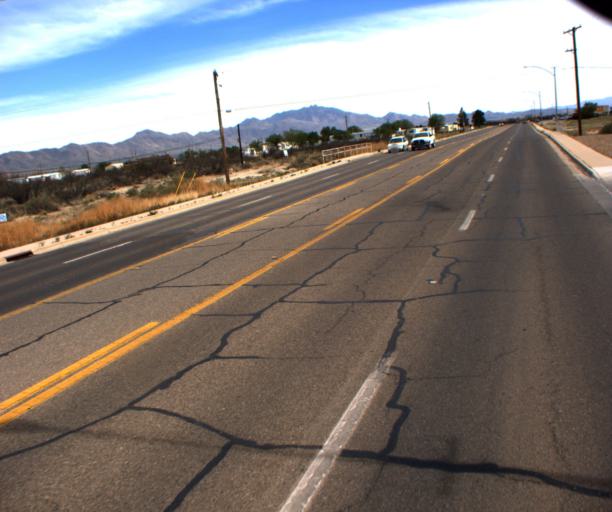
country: US
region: Arizona
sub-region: Cochise County
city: Willcox
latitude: 32.2632
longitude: -109.8299
